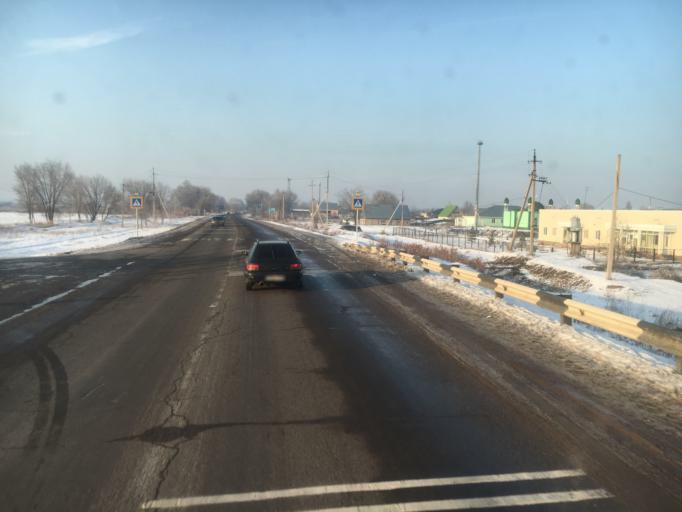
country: KZ
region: Almaty Oblysy
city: Burunday
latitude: 43.3322
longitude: 76.6617
